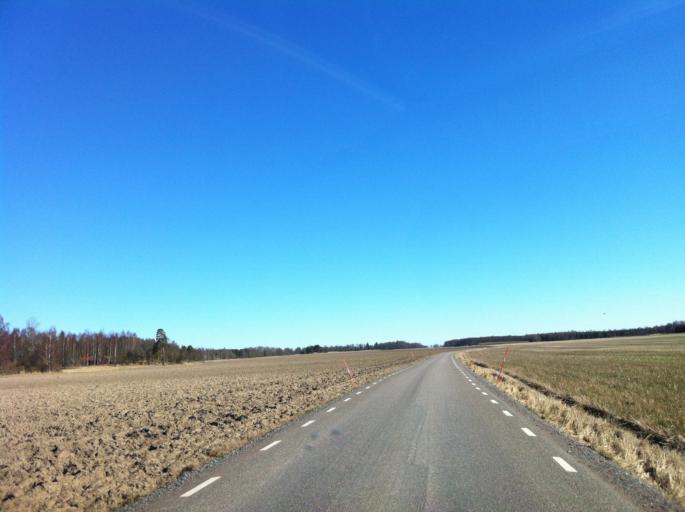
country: SE
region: Vaestra Goetaland
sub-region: Grastorps Kommun
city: Graestorp
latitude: 58.4024
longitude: 12.5737
